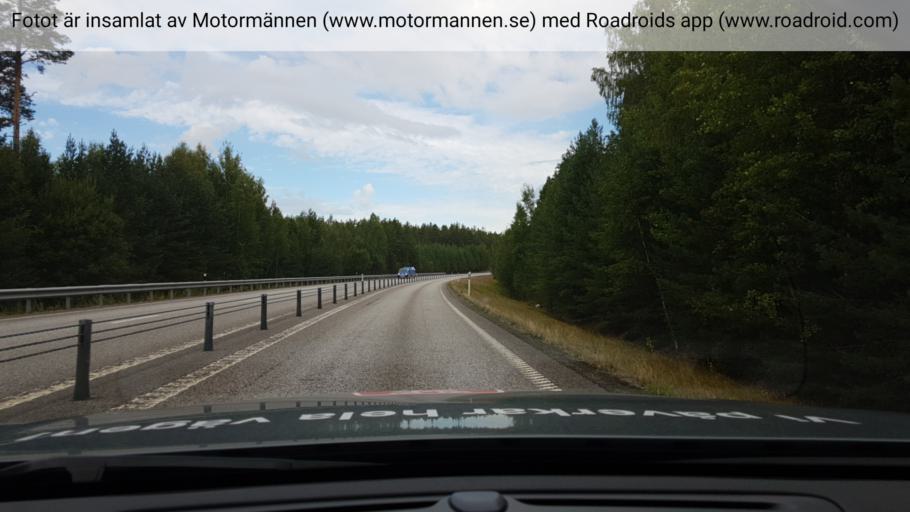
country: SE
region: Uppsala
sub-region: Heby Kommun
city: Tarnsjo
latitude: 60.1803
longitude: 16.9458
